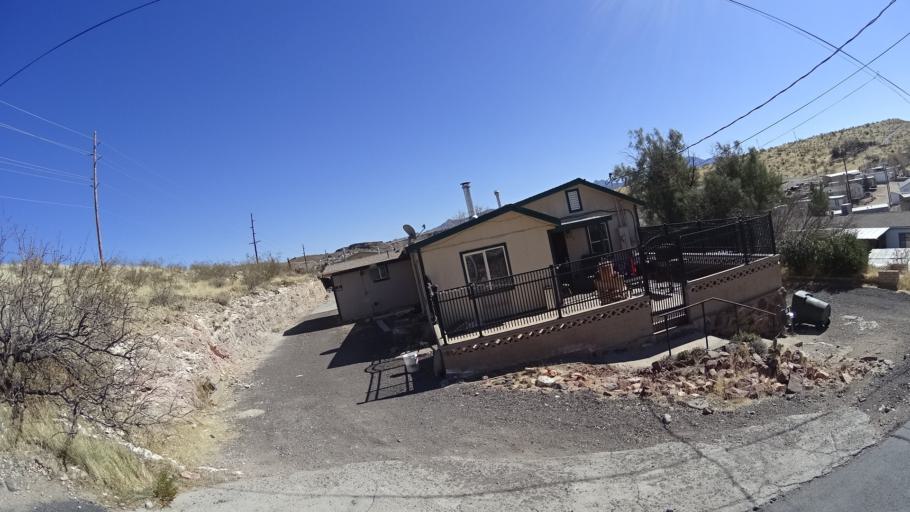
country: US
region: Arizona
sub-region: Mohave County
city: Kingman
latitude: 35.1851
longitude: -114.0552
